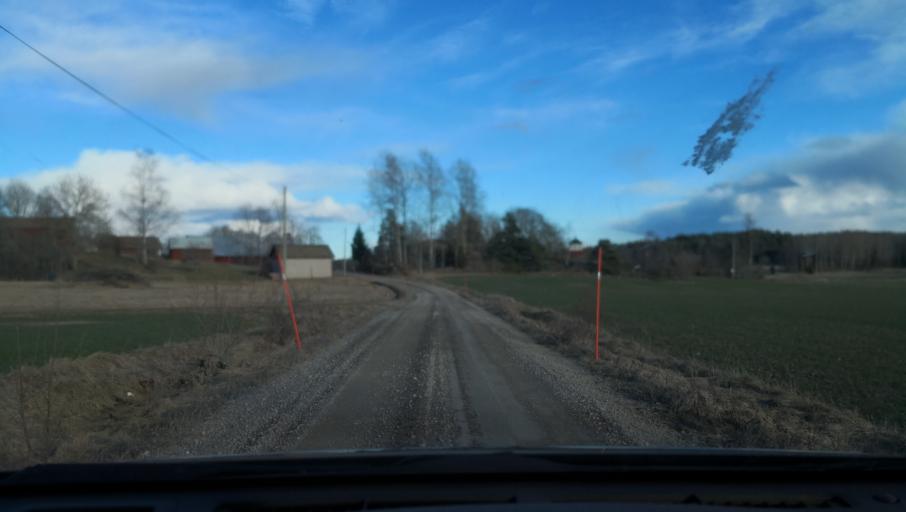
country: SE
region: Vaestmanland
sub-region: Arboga Kommun
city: Arboga
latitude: 59.4476
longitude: 15.7412
